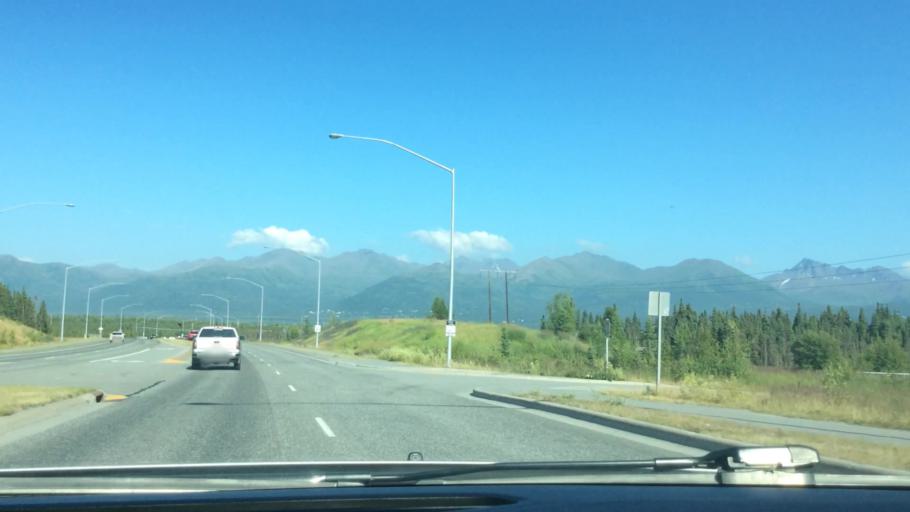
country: US
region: Alaska
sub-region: Anchorage Municipality
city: Anchorage
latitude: 61.1667
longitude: -149.8198
